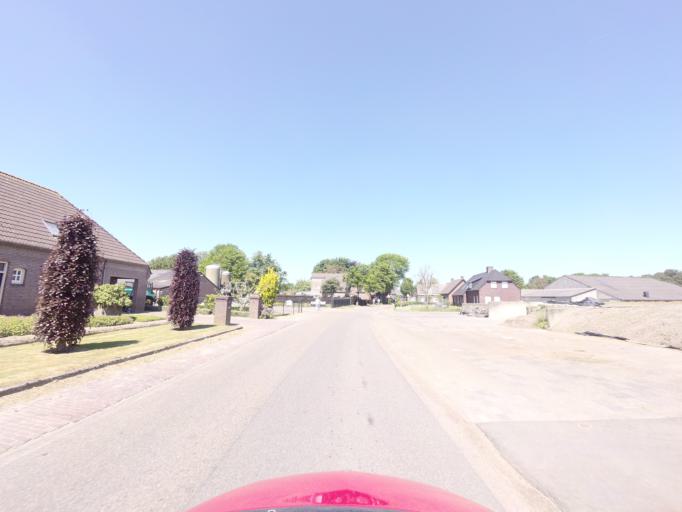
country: NL
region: North Brabant
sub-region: Gemeente Eersel
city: Eersel
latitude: 51.3042
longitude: 5.2985
